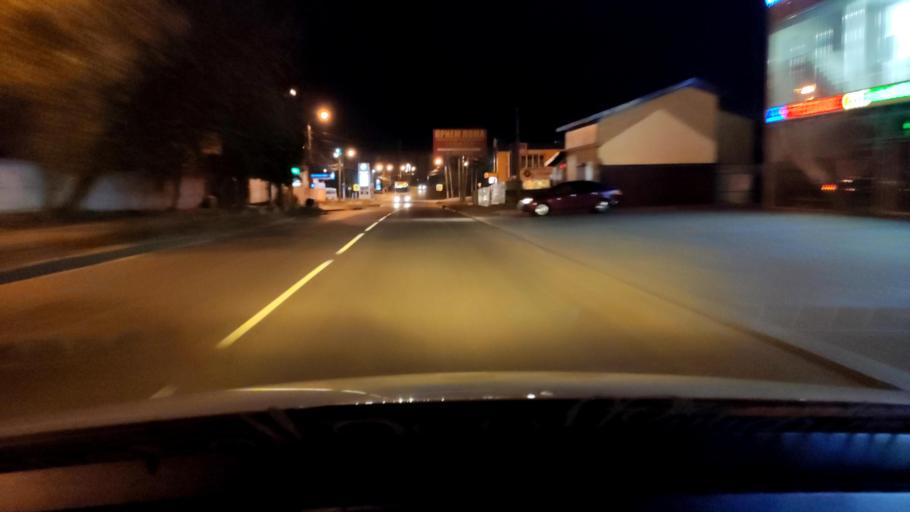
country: RU
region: Voronezj
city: Voronezh
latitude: 51.6627
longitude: 39.1349
